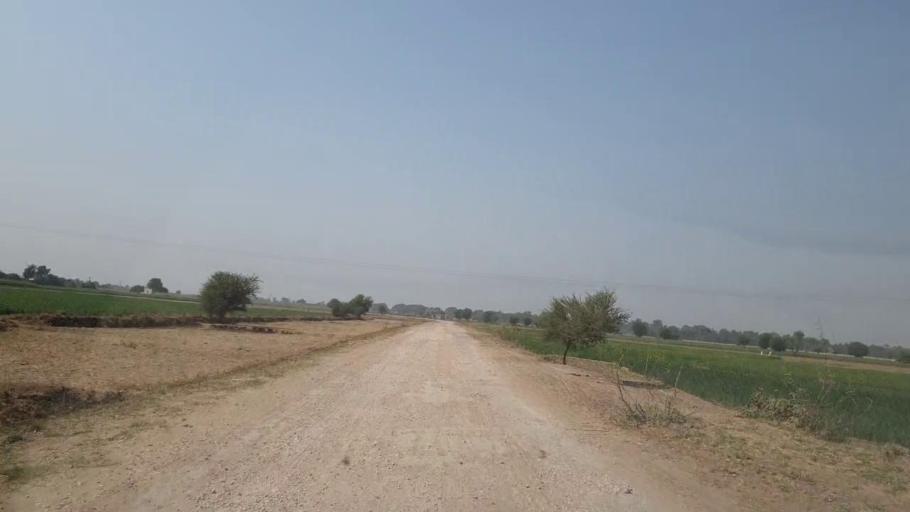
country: PK
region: Sindh
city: Mirpur Khas
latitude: 25.6509
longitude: 69.1084
